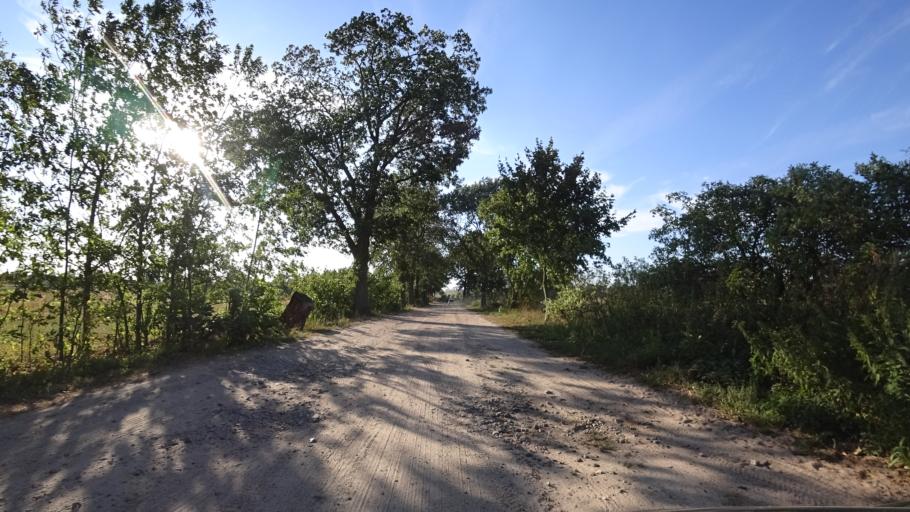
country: DE
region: Brandenburg
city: Stahnsdorf
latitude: 52.3435
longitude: 13.1821
